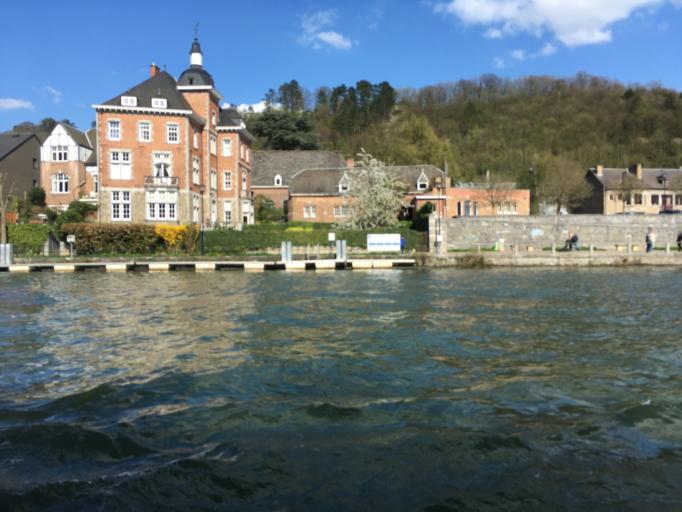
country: BE
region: Wallonia
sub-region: Province de Namur
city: Dinant
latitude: 50.2541
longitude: 4.9143
